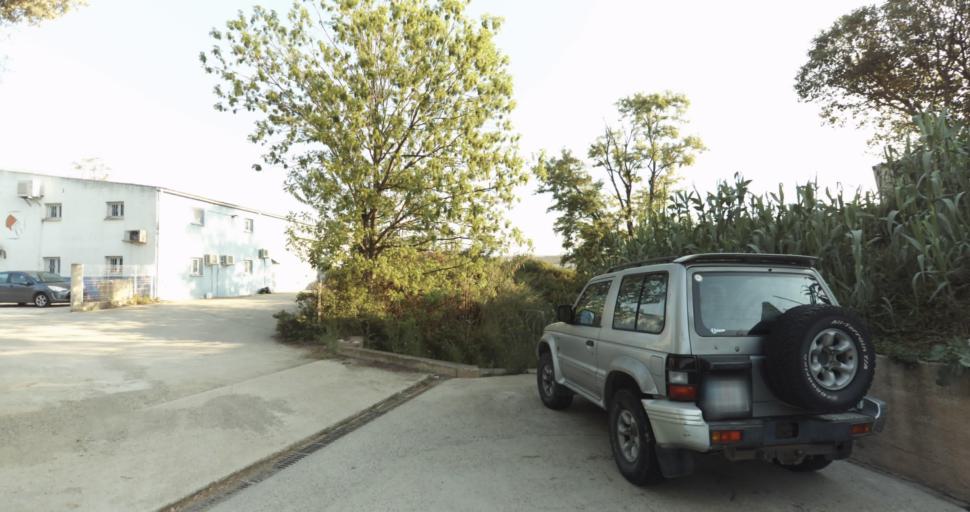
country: FR
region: Corsica
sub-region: Departement de la Haute-Corse
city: Biguglia
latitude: 42.5979
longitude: 9.4410
